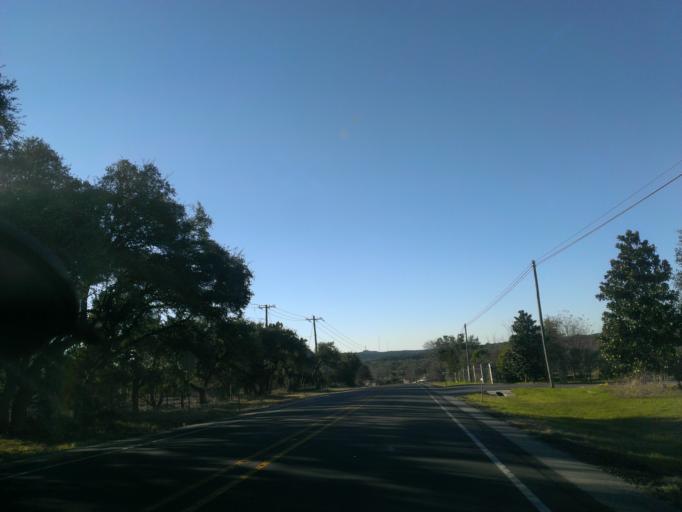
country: US
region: Texas
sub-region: Hays County
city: Dripping Springs
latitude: 30.1276
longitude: -98.0895
